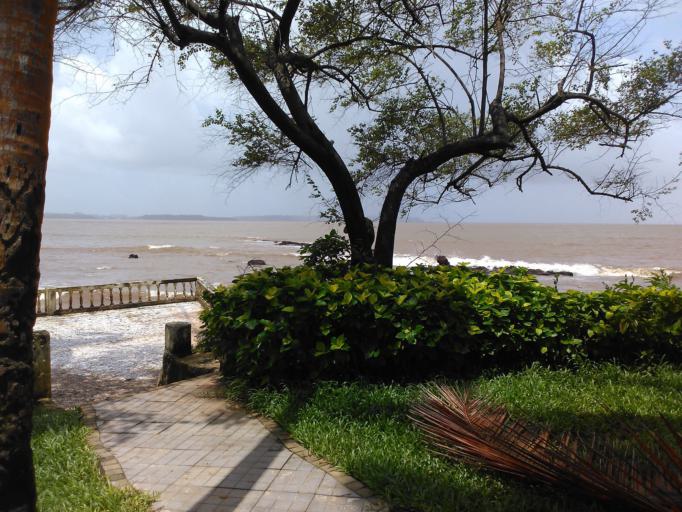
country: IN
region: Goa
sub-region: North Goa
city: Bambolim
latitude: 15.4464
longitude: 73.8538
